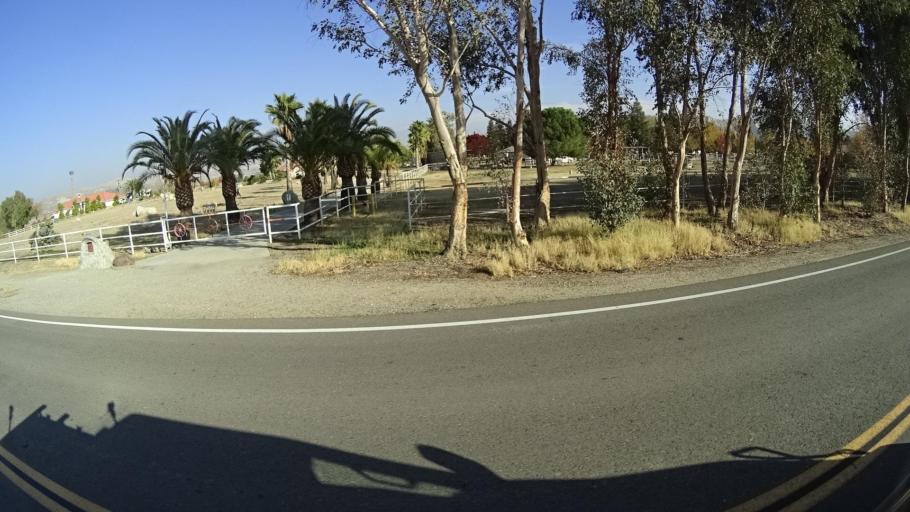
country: US
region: California
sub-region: Kern County
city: Oildale
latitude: 35.4432
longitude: -118.9446
